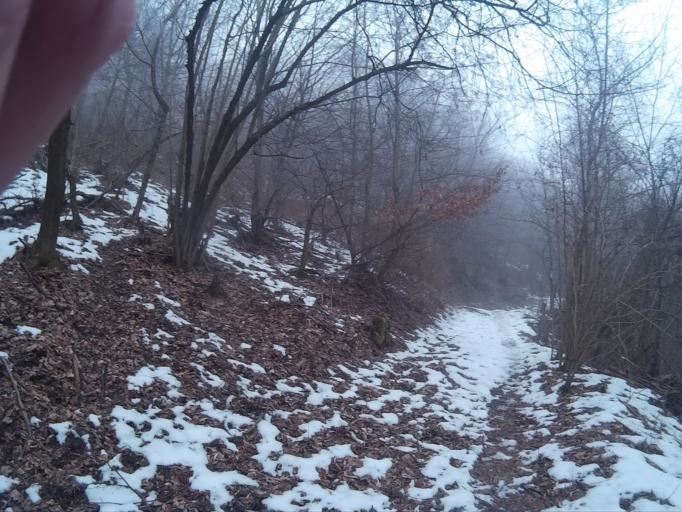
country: HU
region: Nograd
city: Matraverebely
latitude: 47.9827
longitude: 19.7627
